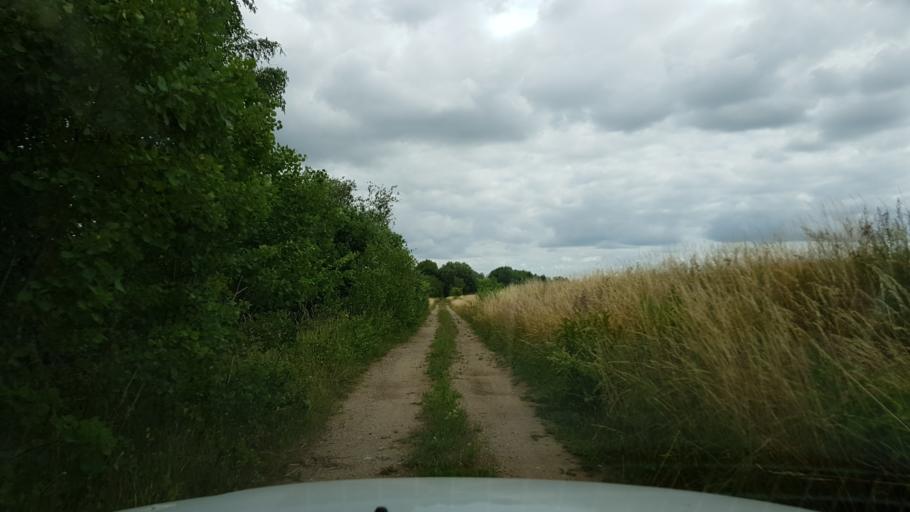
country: PL
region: West Pomeranian Voivodeship
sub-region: Powiat mysliborski
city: Mysliborz
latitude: 52.9398
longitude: 14.9181
